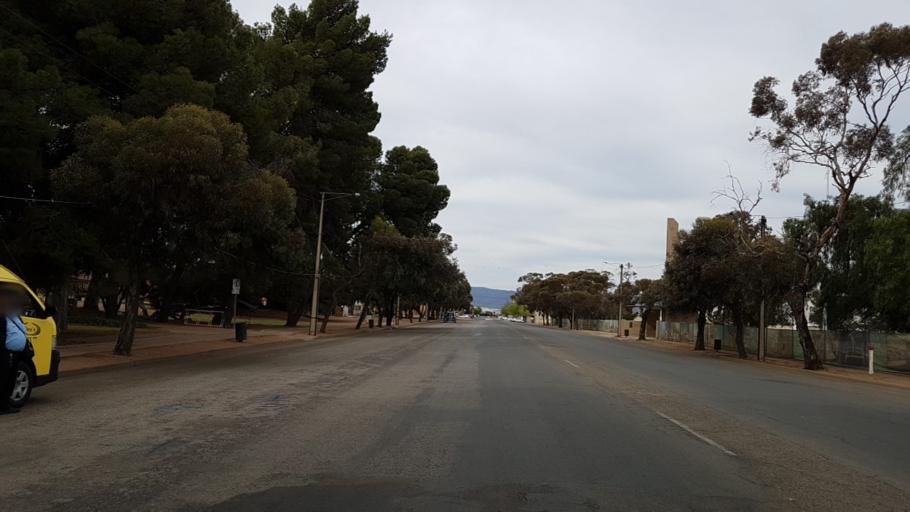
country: AU
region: South Australia
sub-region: Port Pirie City and Dists
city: Port Pirie
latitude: -33.1805
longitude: 138.0057
